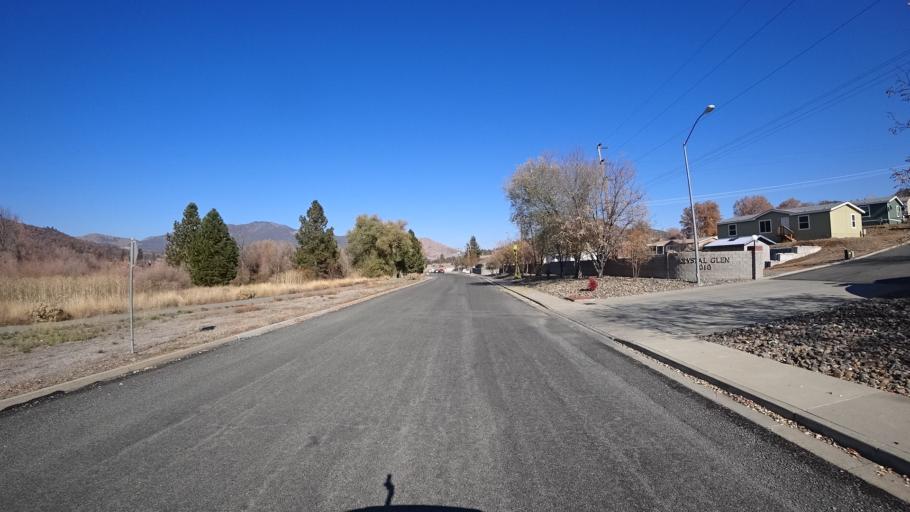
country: US
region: California
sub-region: Siskiyou County
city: Yreka
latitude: 41.7449
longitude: -122.6273
